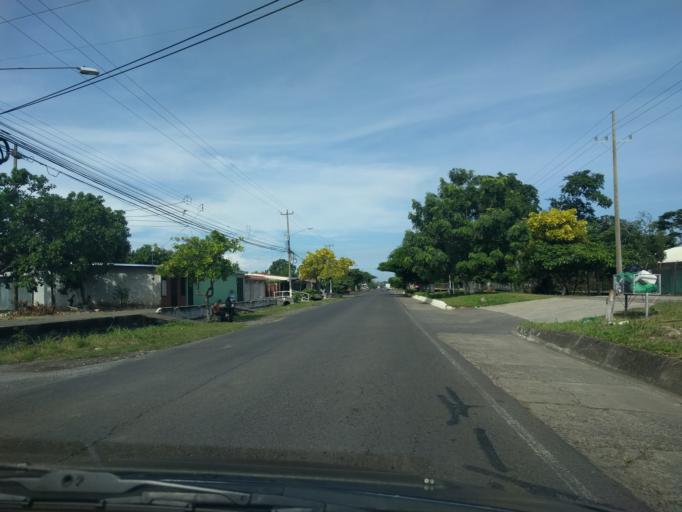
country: CR
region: Puntarenas
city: Esparza
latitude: 9.9855
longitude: -84.7174
